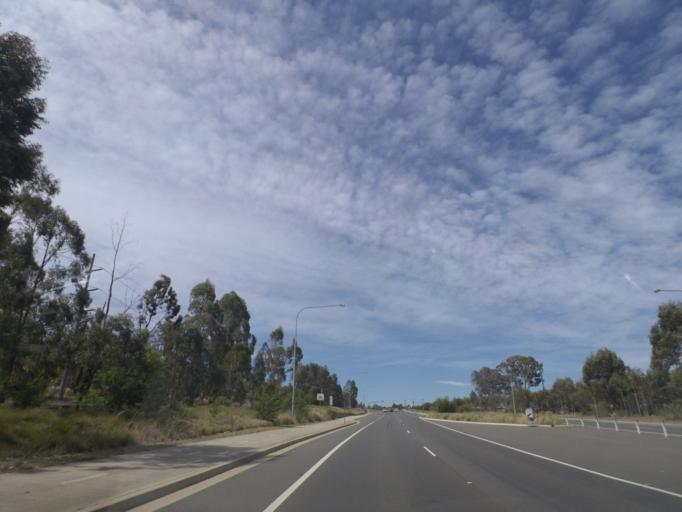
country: AU
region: New South Wales
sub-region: Camden
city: Narellan
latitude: -34.0313
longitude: 150.7506
